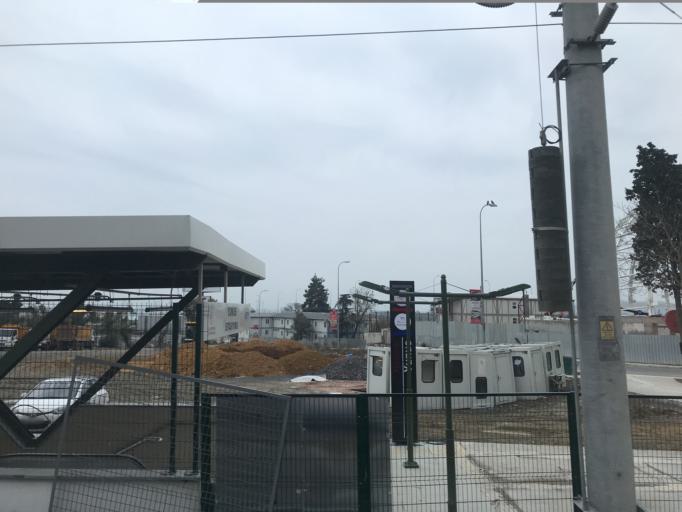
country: TR
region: Istanbul
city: Pendik
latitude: 40.8846
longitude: 29.2101
